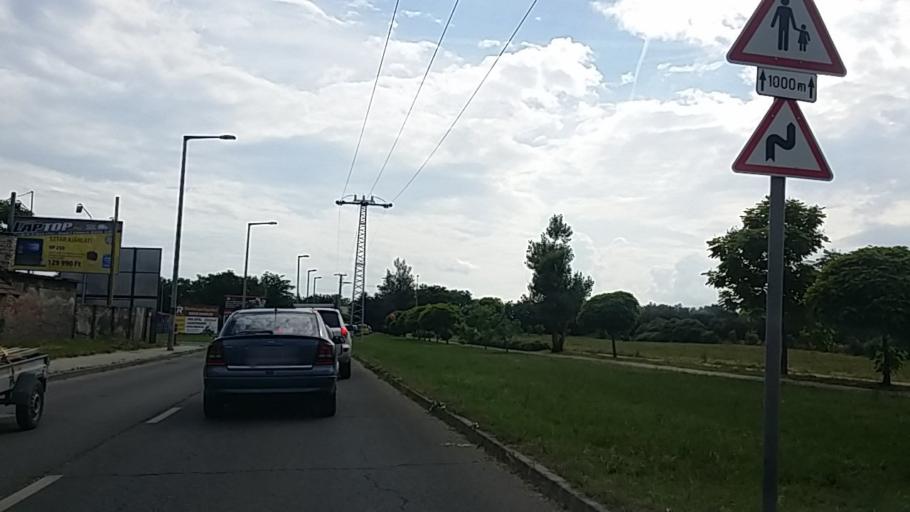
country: HU
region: Budapest
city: Budapest XXI. keruelet
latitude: 47.4039
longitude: 19.0597
